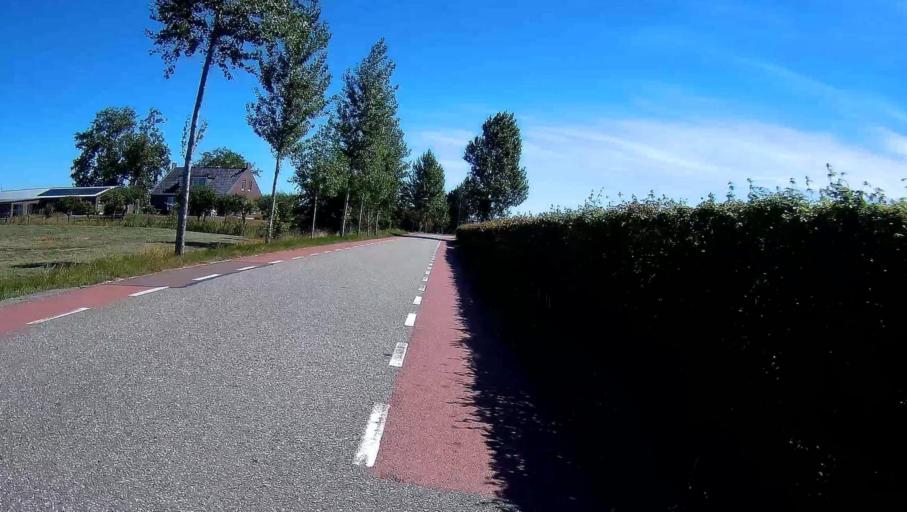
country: NL
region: Utrecht
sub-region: Gemeente IJsselstein
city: IJsselstein
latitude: 52.0560
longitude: 5.0241
